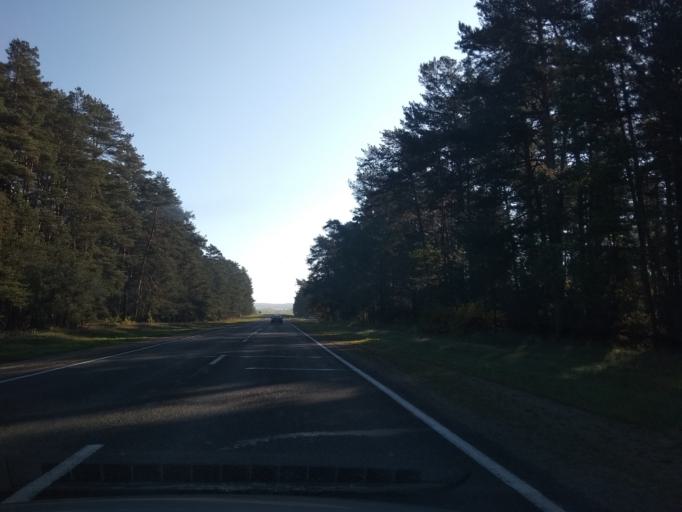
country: BY
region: Grodnenskaya
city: Zel'va
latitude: 53.1465
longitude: 24.8555
